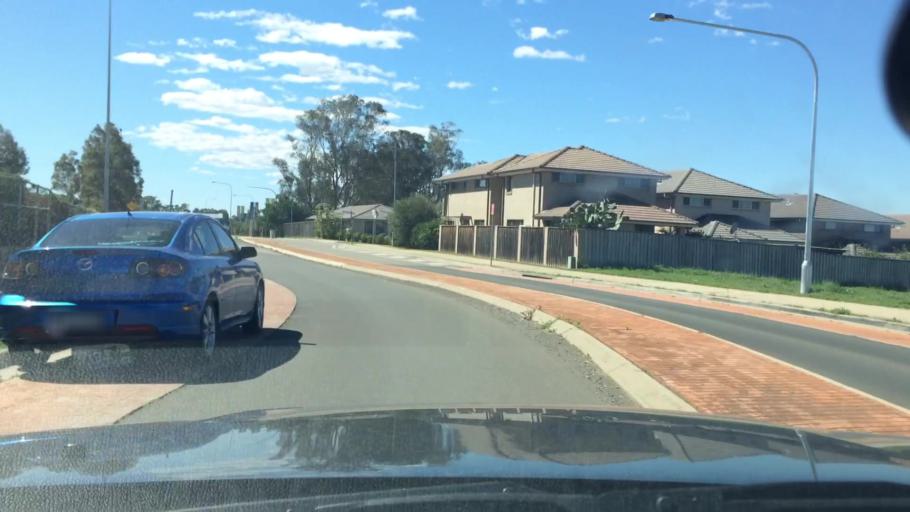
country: AU
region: New South Wales
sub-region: Liverpool
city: Miller
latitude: -33.9381
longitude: 150.8462
